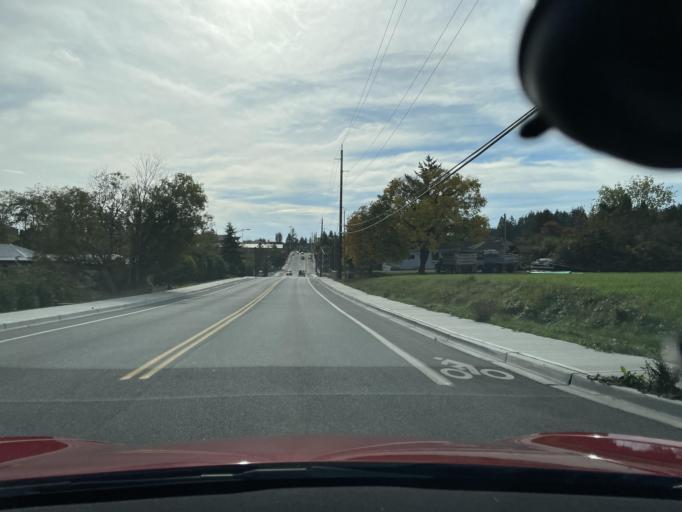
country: US
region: Washington
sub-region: San Juan County
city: Friday Harbor
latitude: 48.5398
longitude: -123.0231
